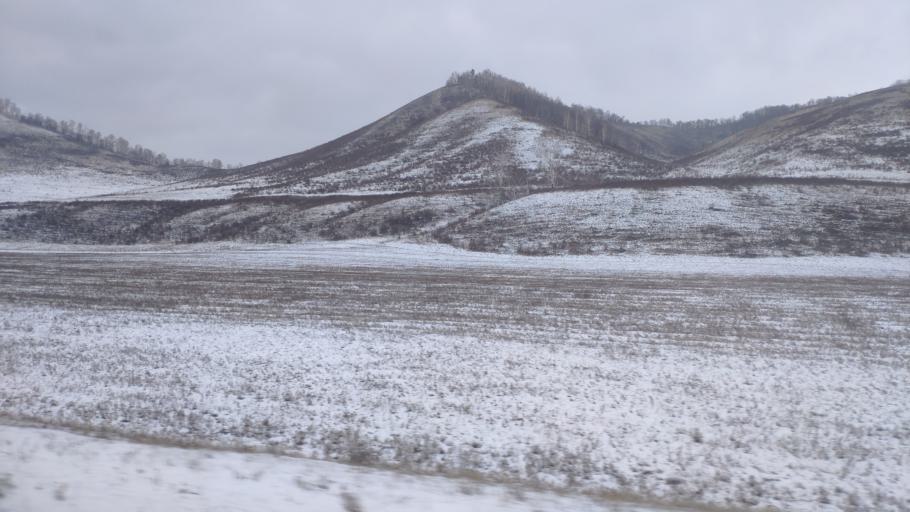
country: RU
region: Bashkortostan
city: Isyangulovo
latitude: 52.1614
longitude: 56.8992
